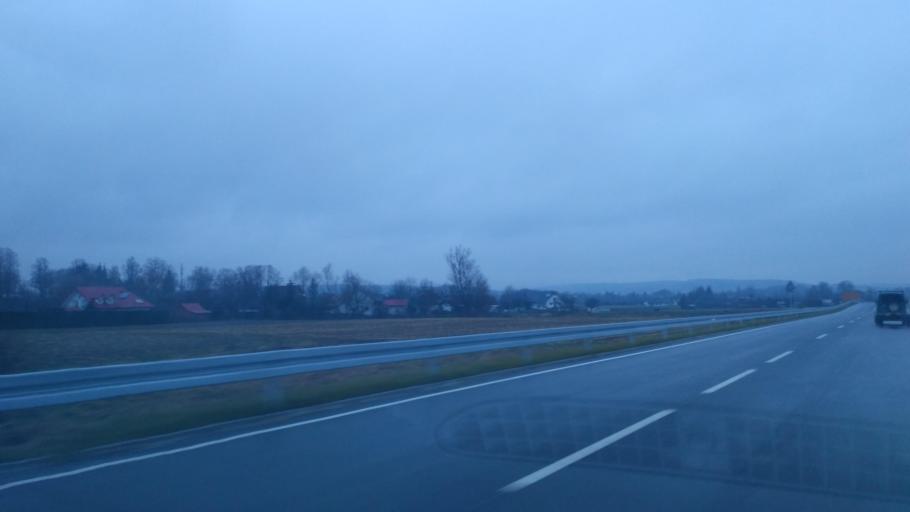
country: PL
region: Subcarpathian Voivodeship
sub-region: Powiat rzeszowski
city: Dynow
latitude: 49.8175
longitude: 22.2408
